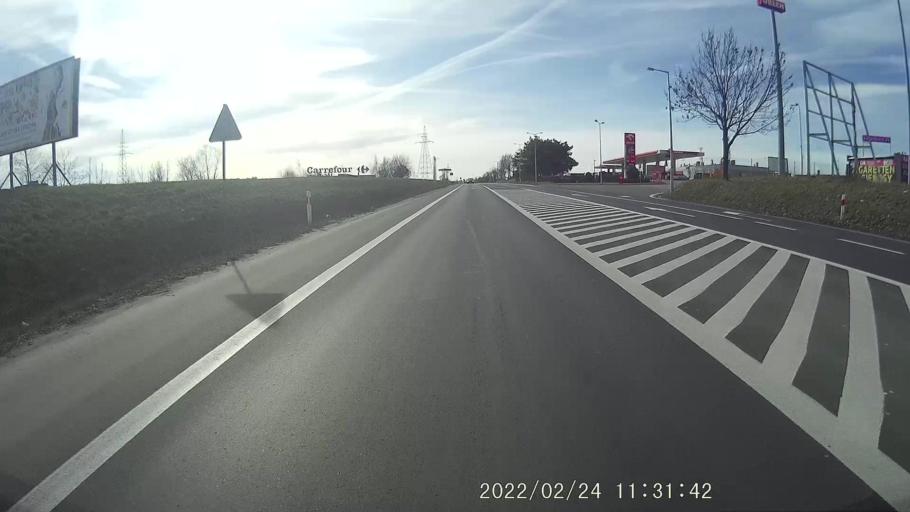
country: PL
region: Lower Silesian Voivodeship
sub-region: Powiat polkowicki
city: Przemkow
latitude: 51.5224
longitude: 15.7364
